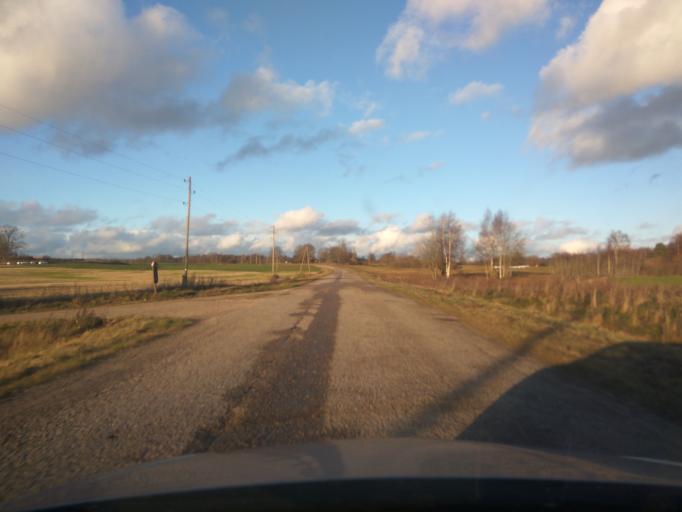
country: LV
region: Aizpute
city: Aizpute
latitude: 56.7664
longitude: 21.7835
